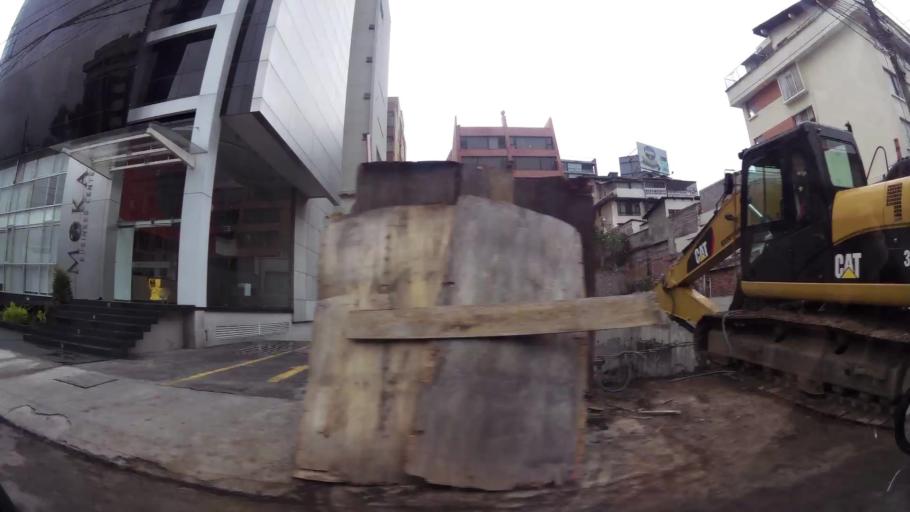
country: EC
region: Pichincha
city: Quito
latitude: -0.1969
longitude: -78.4825
